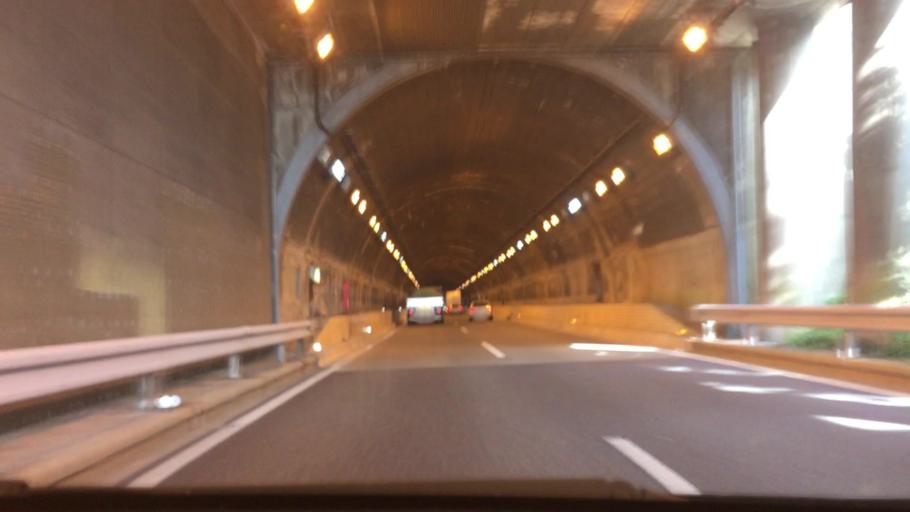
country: JP
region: Yamaguchi
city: Shimonoseki
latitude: 33.9577
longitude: 130.9670
